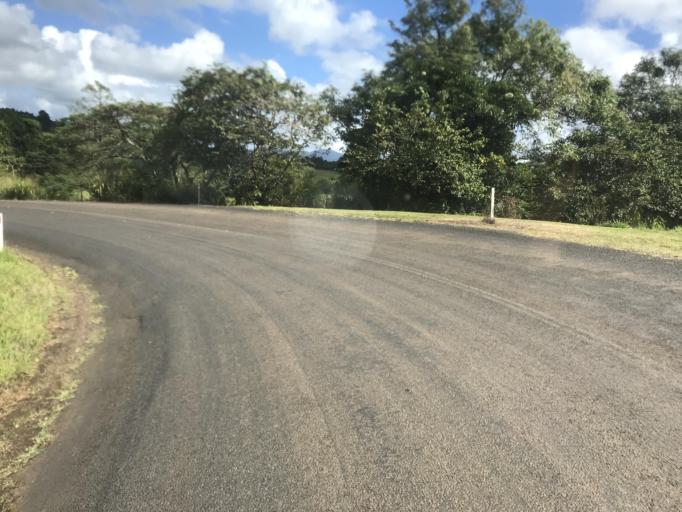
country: AU
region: Queensland
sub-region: Cassowary Coast
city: Innisfail
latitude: -17.5584
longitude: 145.8915
